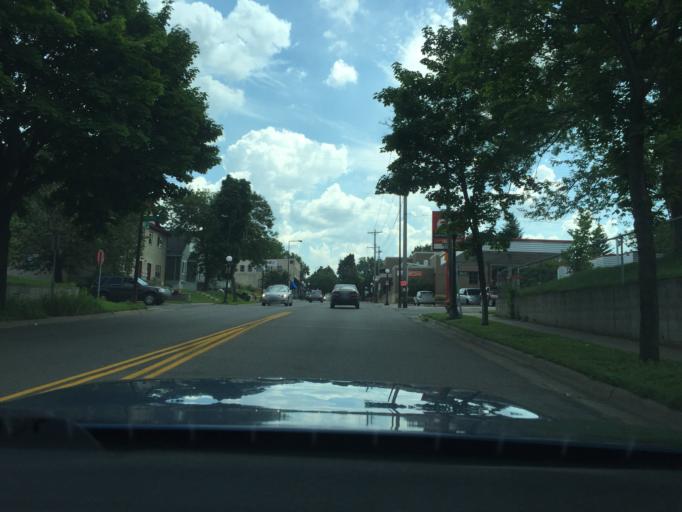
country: US
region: Minnesota
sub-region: Dakota County
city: West Saint Paul
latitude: 44.9289
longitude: -93.1020
